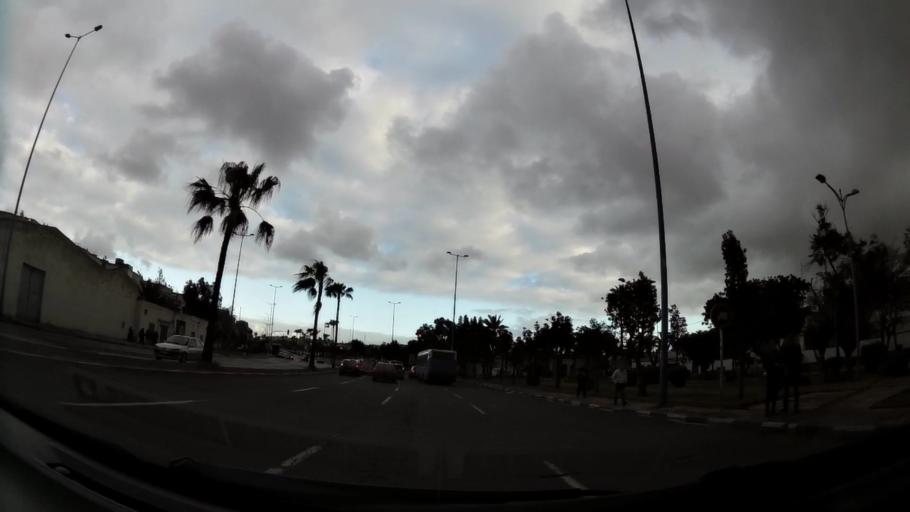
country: MA
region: Grand Casablanca
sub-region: Casablanca
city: Casablanca
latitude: 33.5566
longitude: -7.5939
